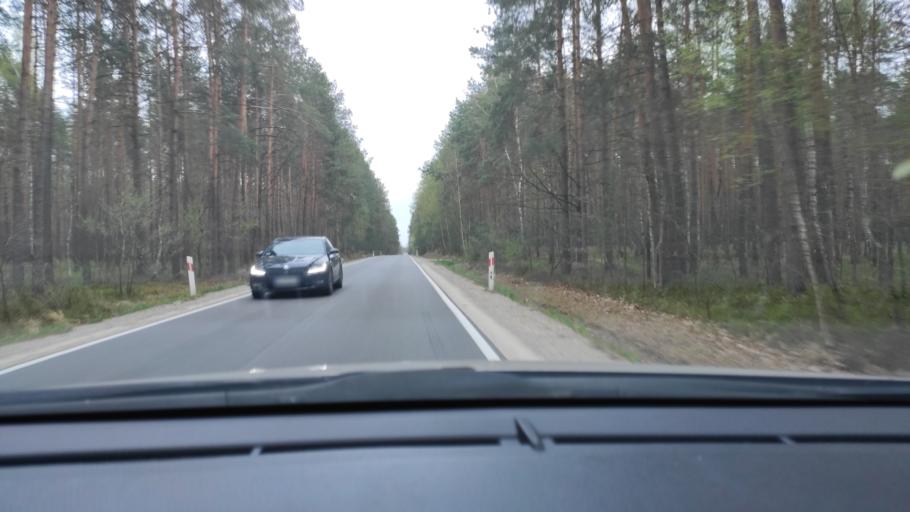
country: PL
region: Masovian Voivodeship
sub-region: Powiat zwolenski
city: Zwolen
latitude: 51.3917
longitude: 21.5479
